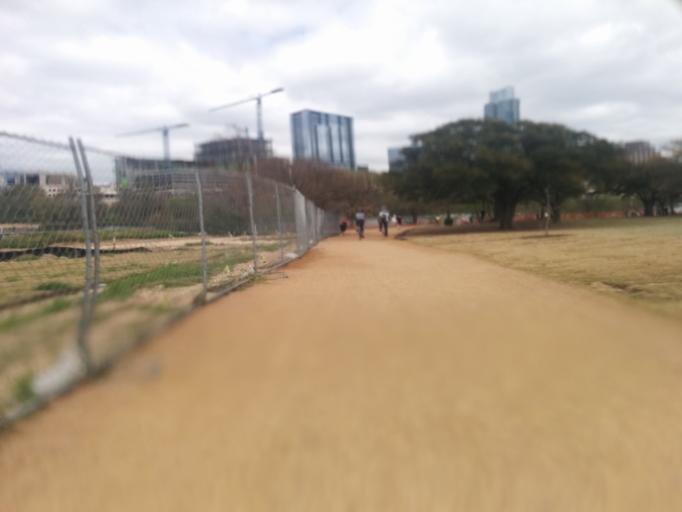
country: US
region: Texas
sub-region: Travis County
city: Austin
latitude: 30.2631
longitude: -97.7522
